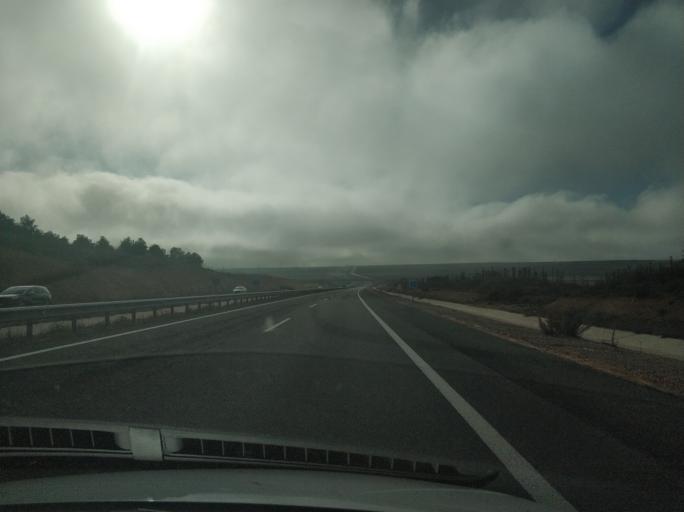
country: ES
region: Castille and Leon
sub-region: Provincia de Soria
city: Adradas
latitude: 41.2904
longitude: -2.4764
